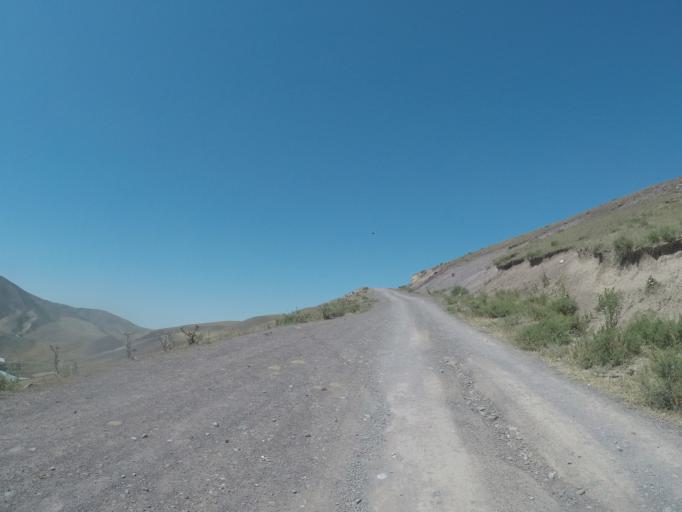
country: KG
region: Chuy
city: Bishkek
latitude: 42.6476
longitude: 74.5147
